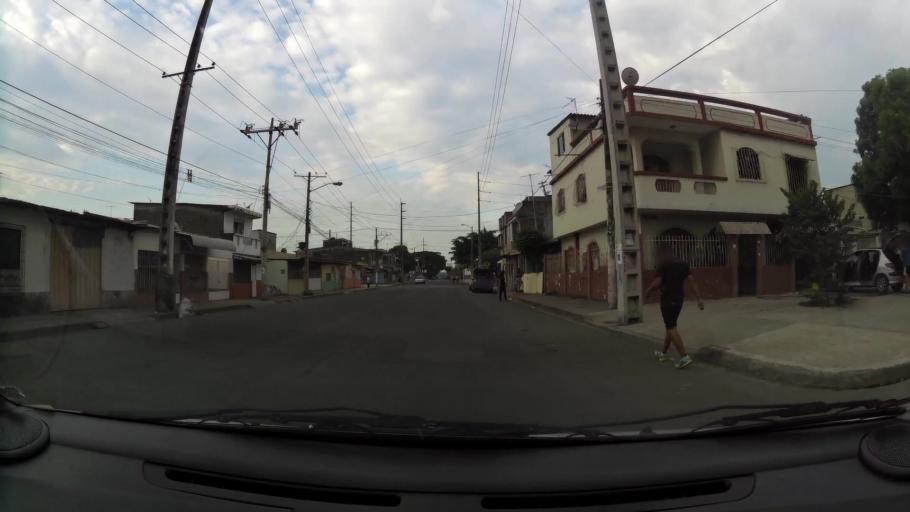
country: EC
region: Guayas
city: Guayaquil
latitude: -2.2509
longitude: -79.8803
